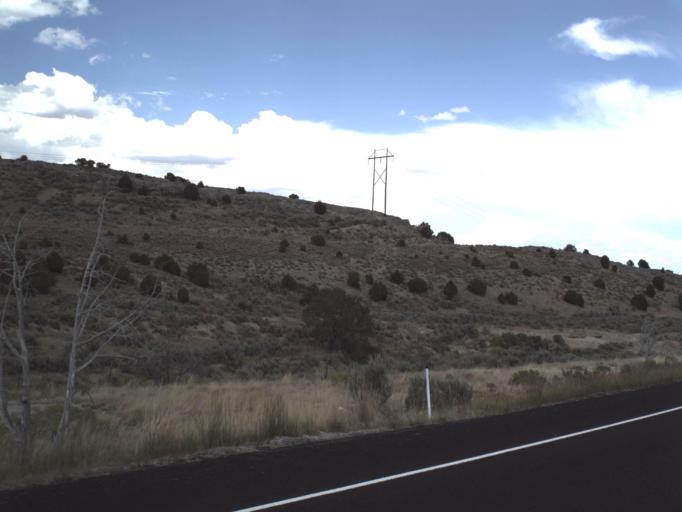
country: US
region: Idaho
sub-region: Minidoka County
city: Rupert
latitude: 41.9736
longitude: -113.1558
